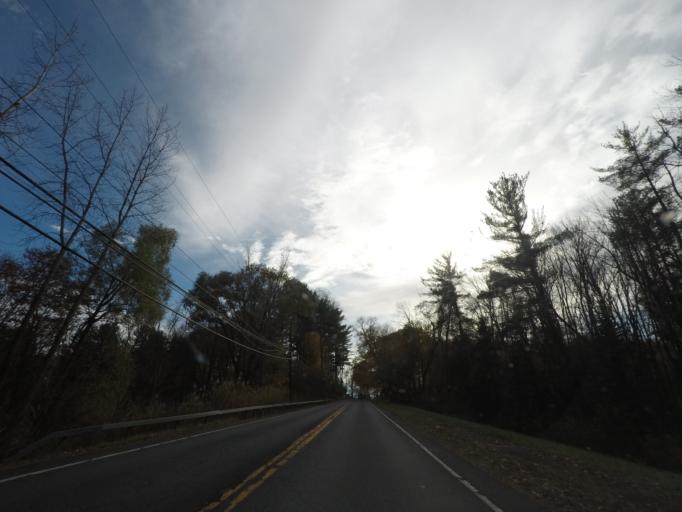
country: US
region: New York
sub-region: Albany County
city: Delmar
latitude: 42.6342
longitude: -73.8572
